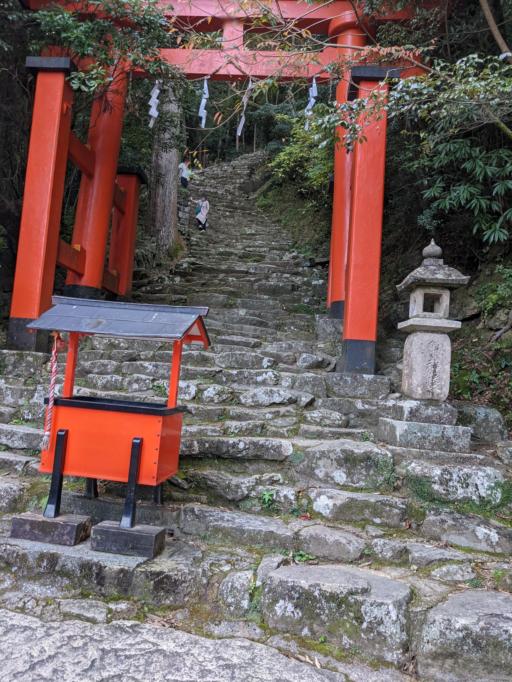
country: JP
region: Wakayama
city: Shingu
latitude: 33.7240
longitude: 135.9841
